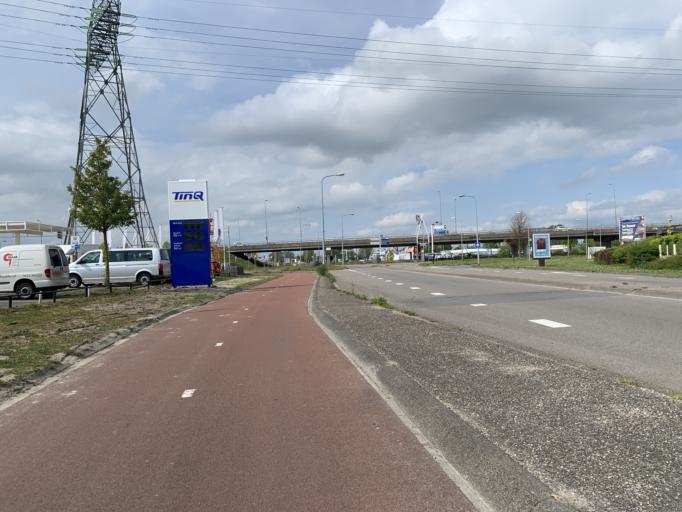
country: NL
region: Groningen
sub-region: Gemeente Groningen
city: Oosterpark
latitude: 53.2119
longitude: 6.5951
